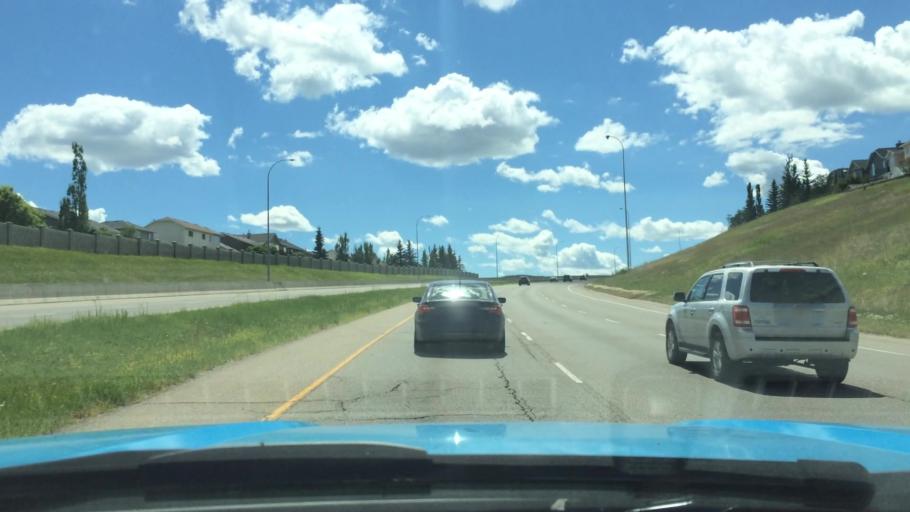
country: CA
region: Alberta
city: Calgary
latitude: 51.1350
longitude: -114.1220
